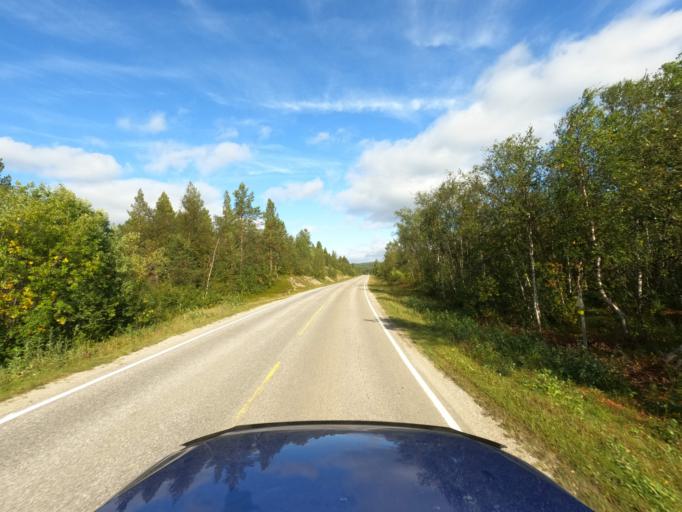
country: NO
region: Finnmark Fylke
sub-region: Porsanger
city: Lakselv
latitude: 69.8963
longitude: 24.9927
